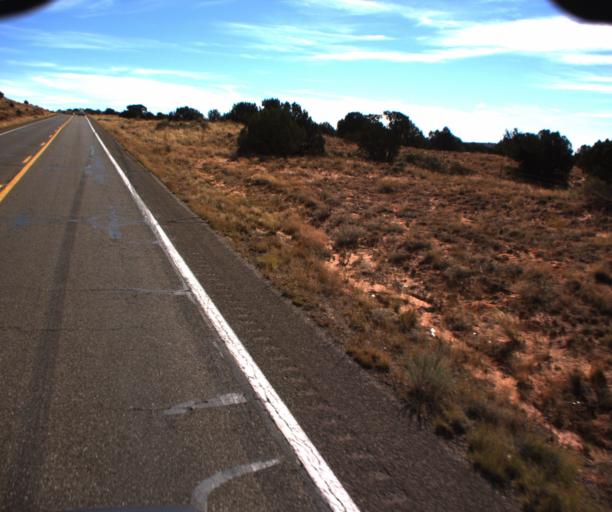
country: US
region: Arizona
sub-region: Coconino County
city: Kaibito
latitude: 36.5778
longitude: -111.1301
